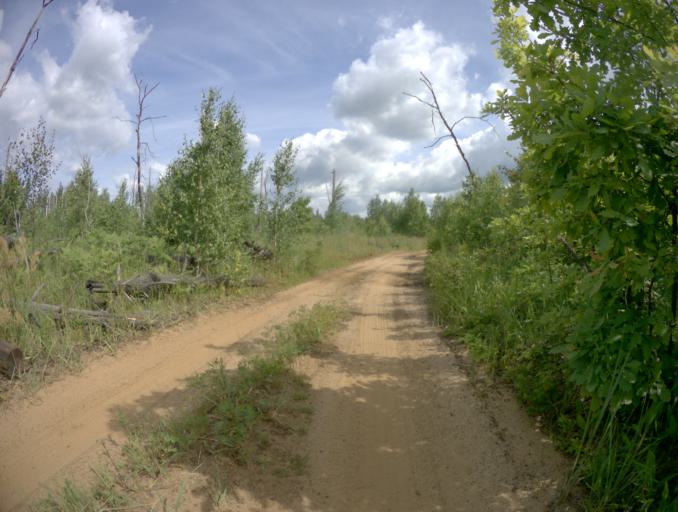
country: RU
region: Ivanovo
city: Talitsy
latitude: 56.5320
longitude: 42.4624
